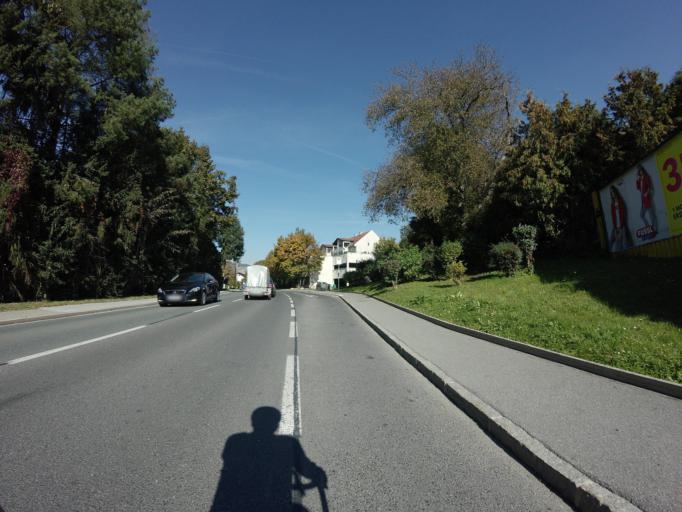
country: AT
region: Styria
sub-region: Politischer Bezirk Graz-Umgebung
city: Stattegg
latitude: 47.1114
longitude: 15.4313
